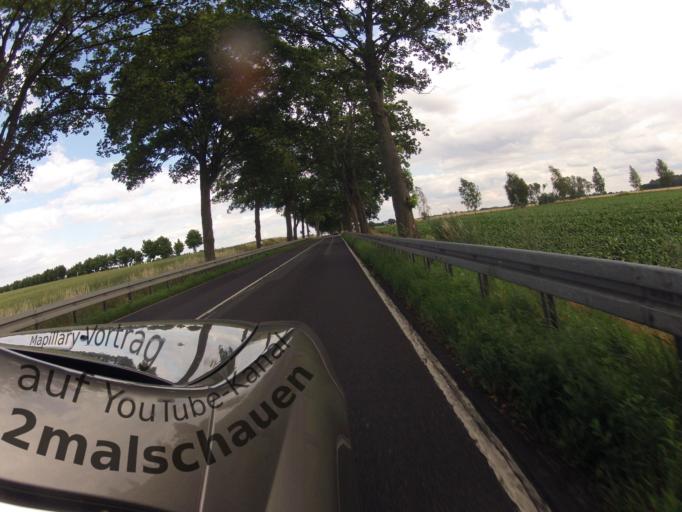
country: DE
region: Mecklenburg-Vorpommern
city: Seebad Bansin
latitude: 53.9029
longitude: 14.0464
